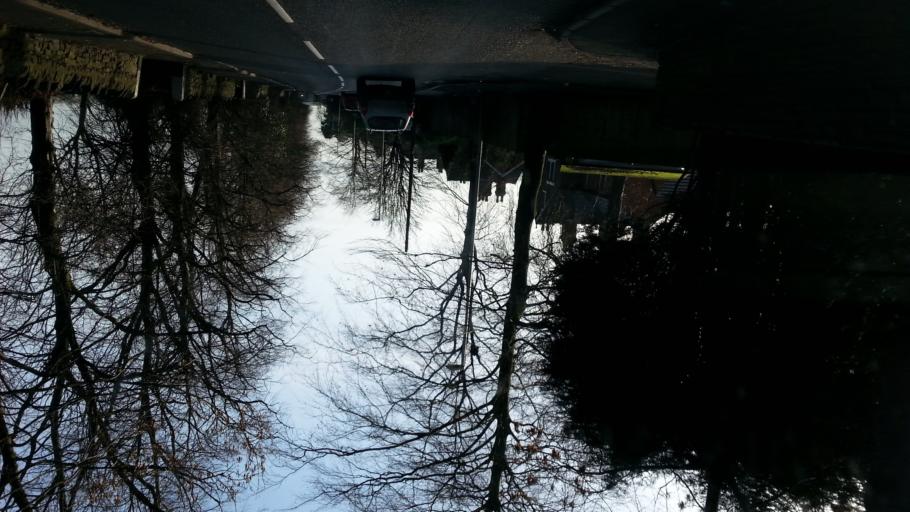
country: GB
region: England
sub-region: Staffordshire
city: Biddulph
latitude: 53.0672
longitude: -2.1208
